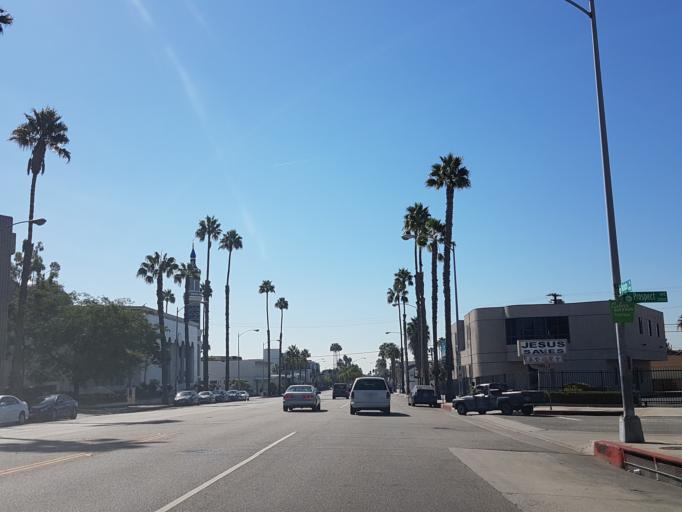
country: US
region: California
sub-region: Los Angeles County
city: Culver City
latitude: 34.0124
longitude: -118.4102
